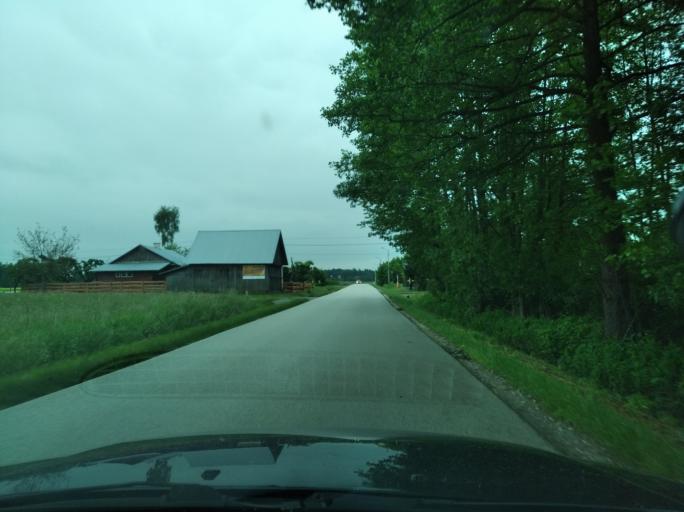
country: PL
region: Subcarpathian Voivodeship
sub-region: Powiat ropczycko-sedziszowski
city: Sedziszow Malopolski
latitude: 50.1236
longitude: 21.6727
